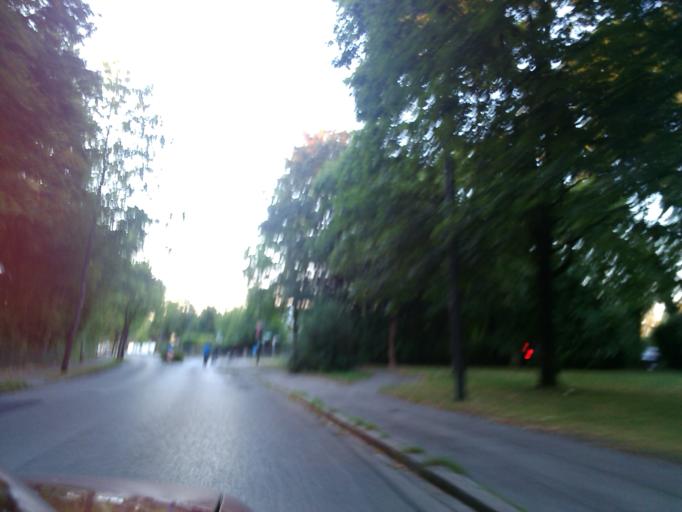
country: DE
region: Bavaria
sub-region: Upper Bavaria
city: Grafelfing
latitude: 48.1122
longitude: 11.4291
